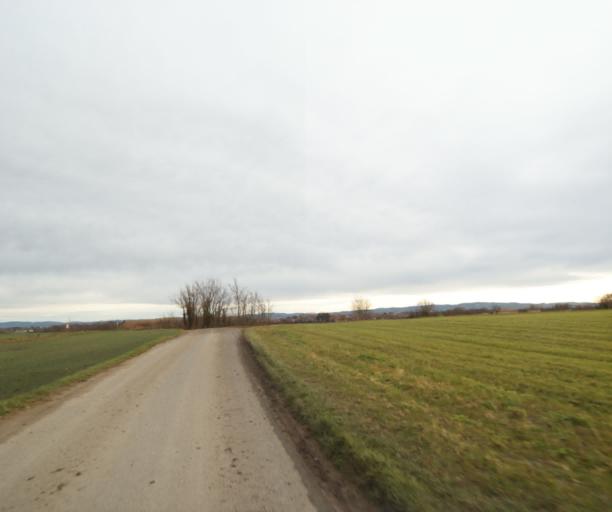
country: FR
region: Rhone-Alpes
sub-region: Departement de la Loire
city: Sury-le-Comtal
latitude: 45.5256
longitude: 4.1672
